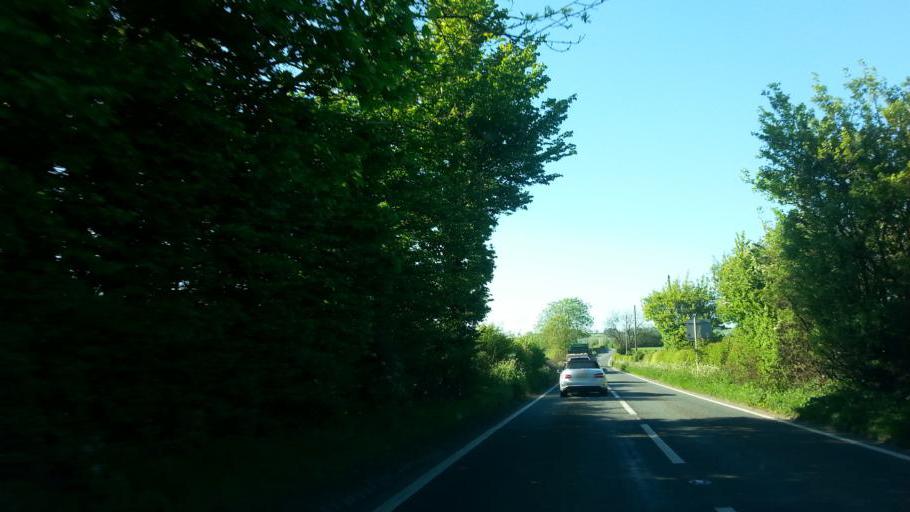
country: GB
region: England
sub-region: Somerset
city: Evercreech
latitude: 51.1453
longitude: -2.5213
